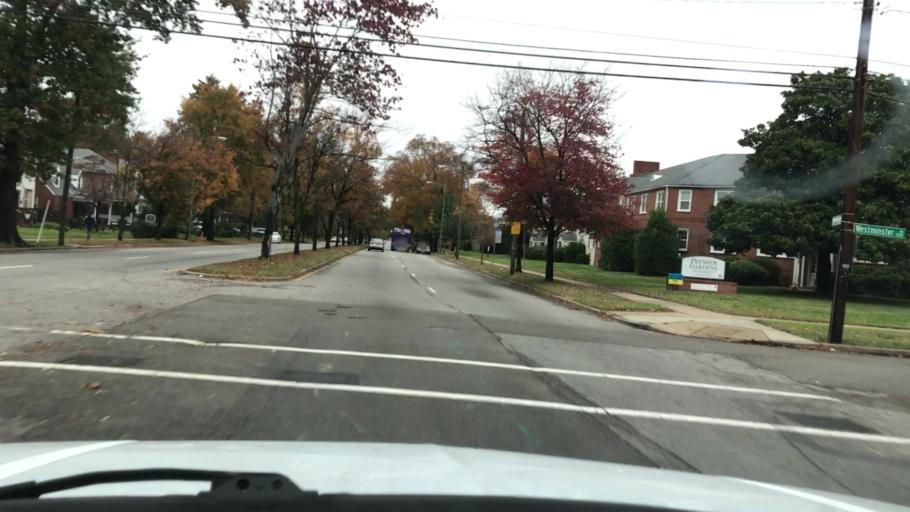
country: US
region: Virginia
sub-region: Henrico County
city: Lakeside
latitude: 37.5943
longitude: -77.4489
